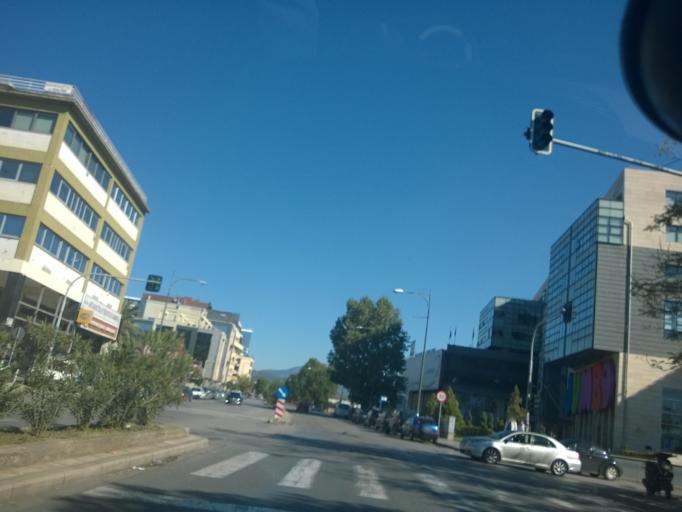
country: GR
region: Central Macedonia
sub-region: Nomos Thessalonikis
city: Thessaloniki
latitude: 40.6410
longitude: 22.9181
